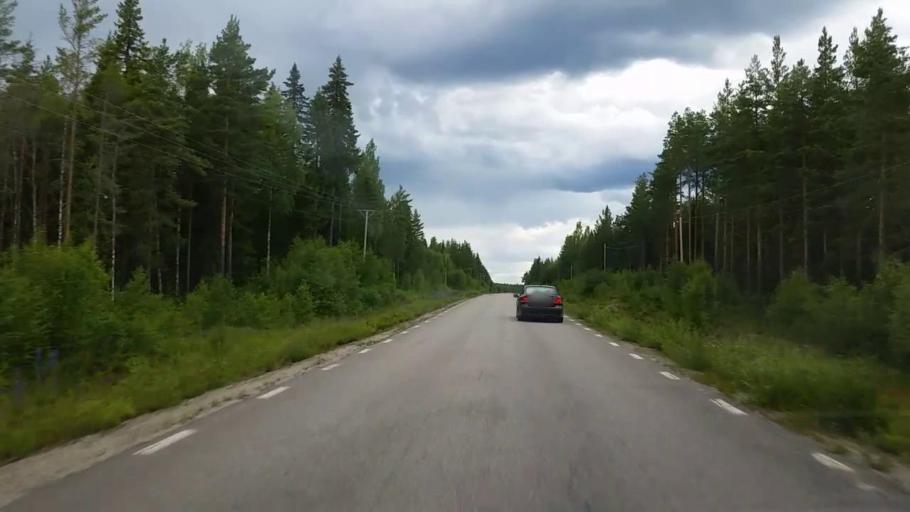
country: SE
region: Gaevleborg
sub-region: Ovanakers Kommun
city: Edsbyn
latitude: 61.4637
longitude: 15.8710
